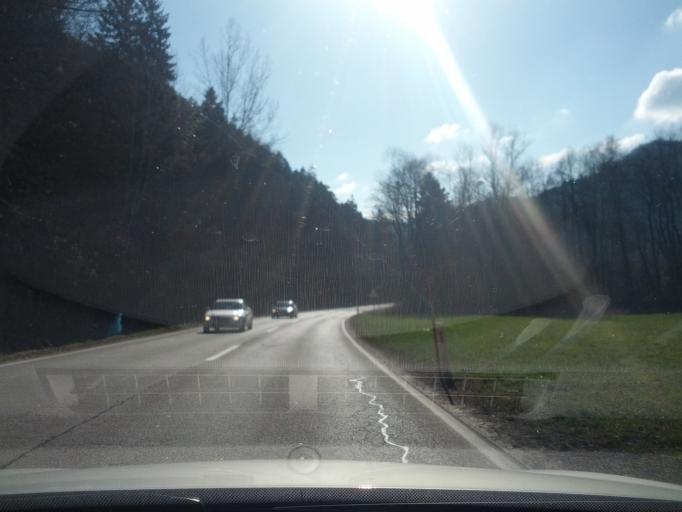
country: SI
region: Moravce
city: Moravce
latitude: 46.0950
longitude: 14.6924
